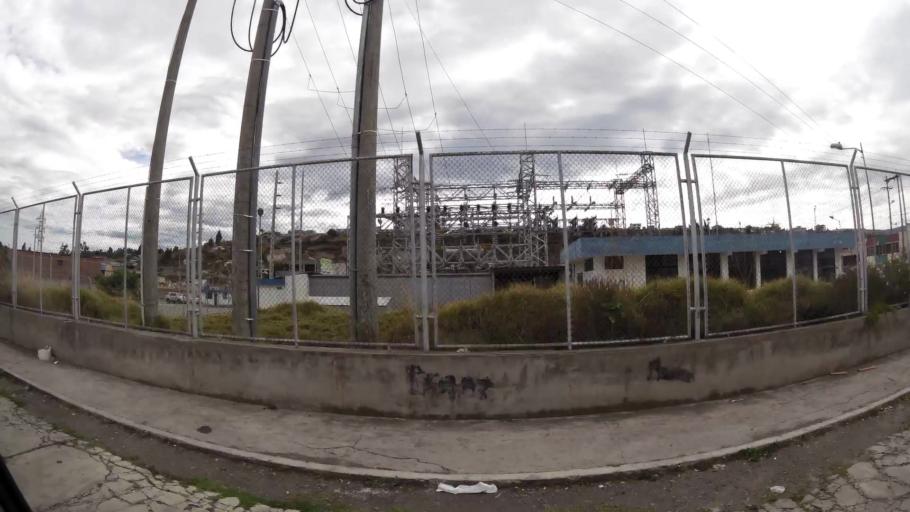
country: EC
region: Cotopaxi
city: Latacunga
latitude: -0.9368
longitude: -78.6229
